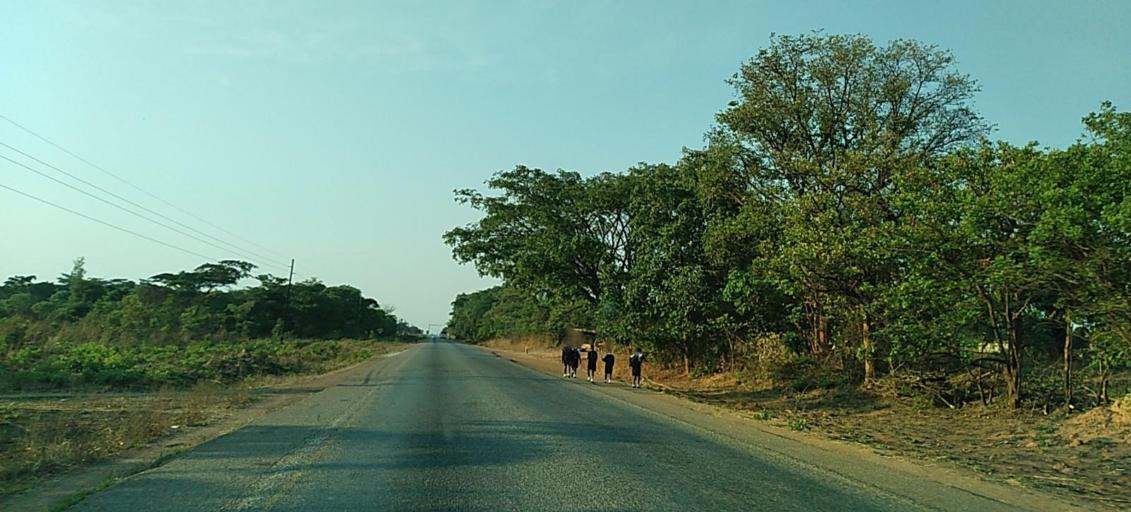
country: ZM
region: Copperbelt
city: Luanshya
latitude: -13.2378
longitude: 28.6789
